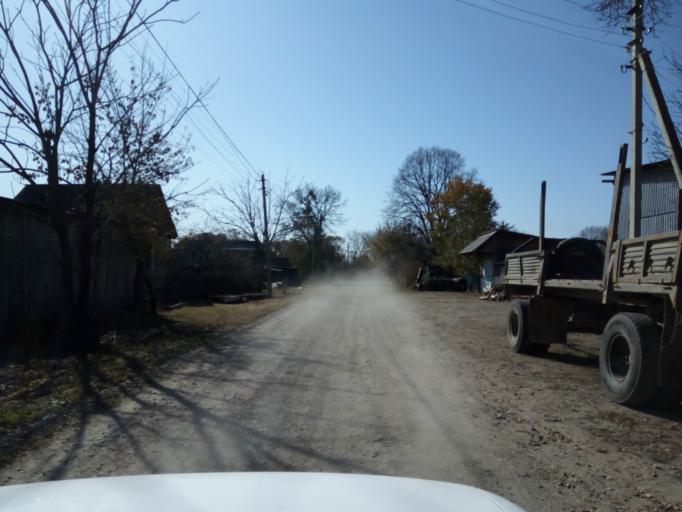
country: RU
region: Primorskiy
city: Dal'nerechensk
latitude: 45.9086
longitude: 133.7948
